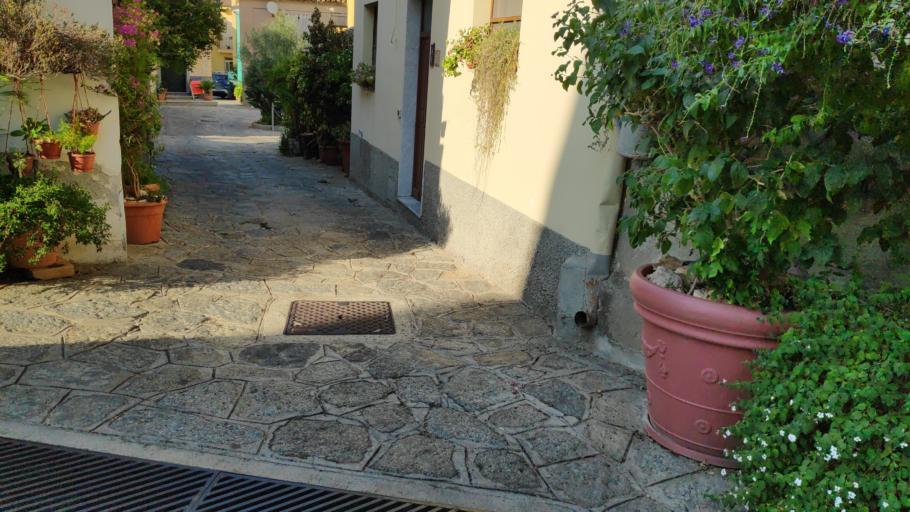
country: IT
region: Calabria
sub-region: Provincia di Catanzaro
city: Soverato Superiore
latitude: 38.6885
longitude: 16.5317
